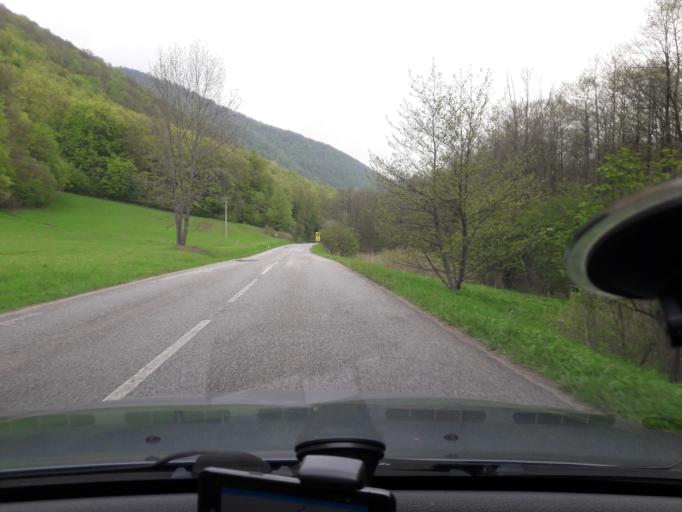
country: SK
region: Banskobystricky
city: Tisovec
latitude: 48.7146
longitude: 20.0026
